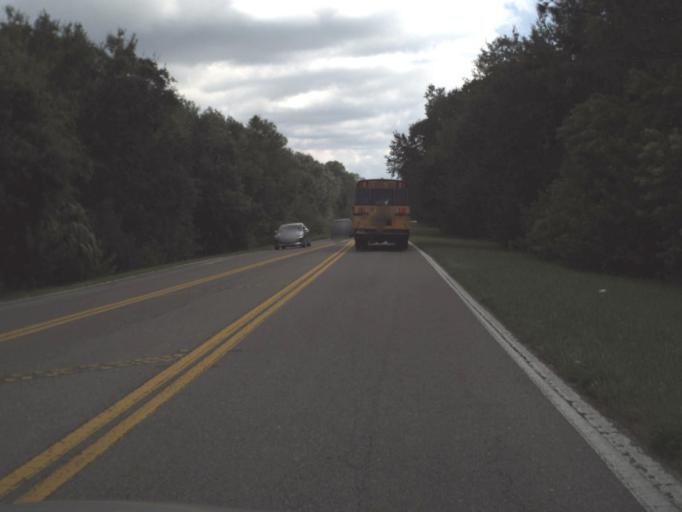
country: US
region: Florida
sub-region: Sarasota County
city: Plantation
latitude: 27.0665
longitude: -82.3207
